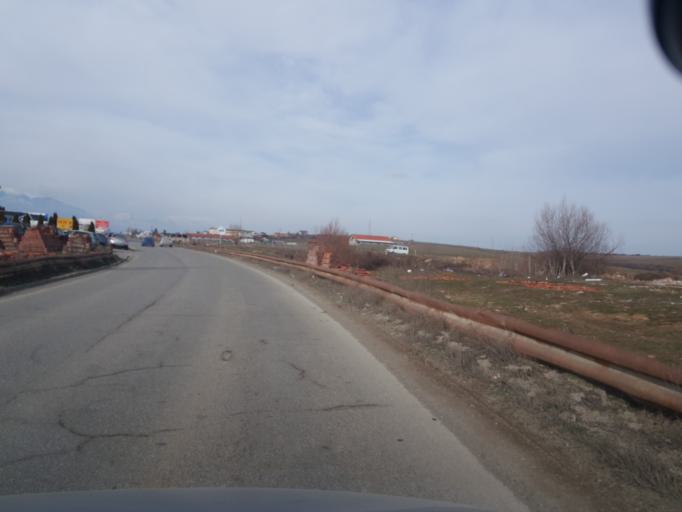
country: XK
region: Gjakova
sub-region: Komuna e Gjakoves
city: Gjakove
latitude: 42.3941
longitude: 20.4442
